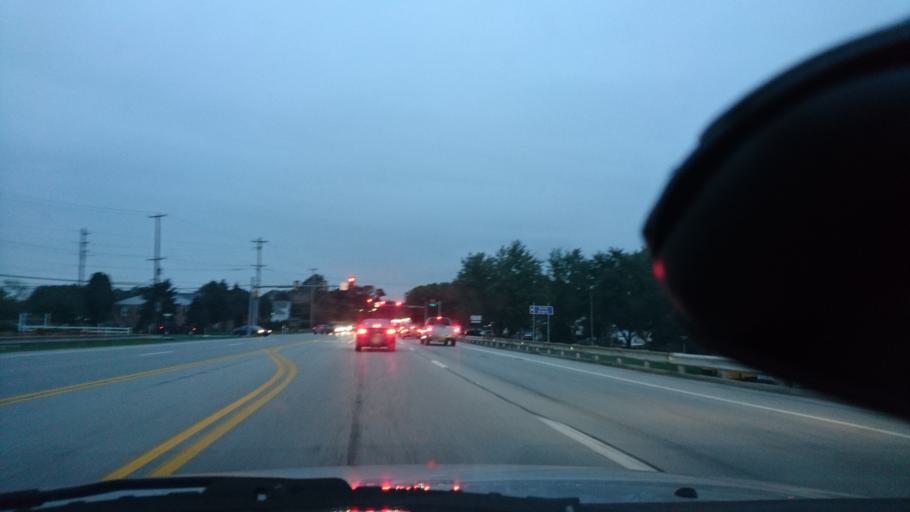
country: US
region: Pennsylvania
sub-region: Delaware County
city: Brookhaven
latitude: 39.8866
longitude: -75.4021
